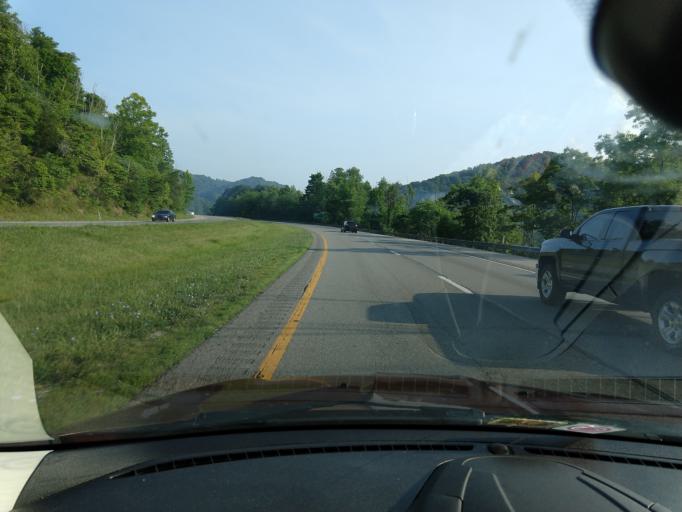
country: US
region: West Virginia
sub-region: Kanawha County
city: Sissonville
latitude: 38.5549
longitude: -81.6336
